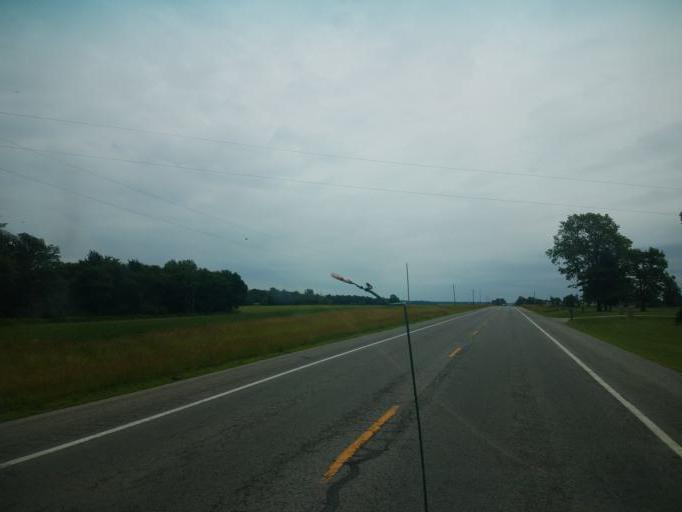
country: US
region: Ohio
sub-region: Hardin County
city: Kenton
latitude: 40.6887
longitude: -83.6902
